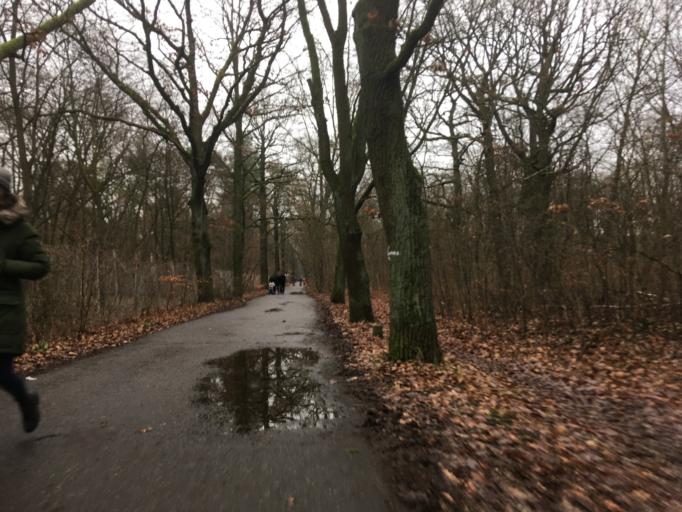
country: DE
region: Berlin
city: Oberschoneweide
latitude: 52.4639
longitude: 13.5359
